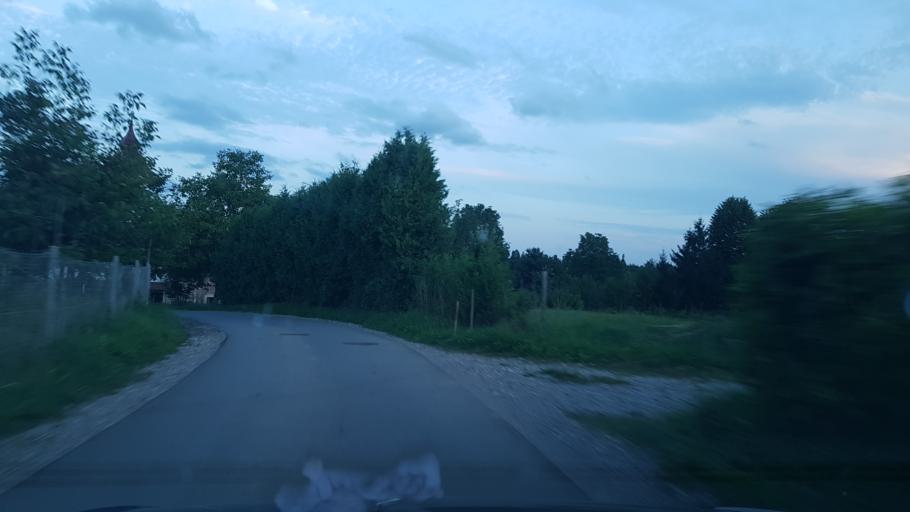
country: SI
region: Postojna
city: Postojna
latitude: 45.7426
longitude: 14.1842
